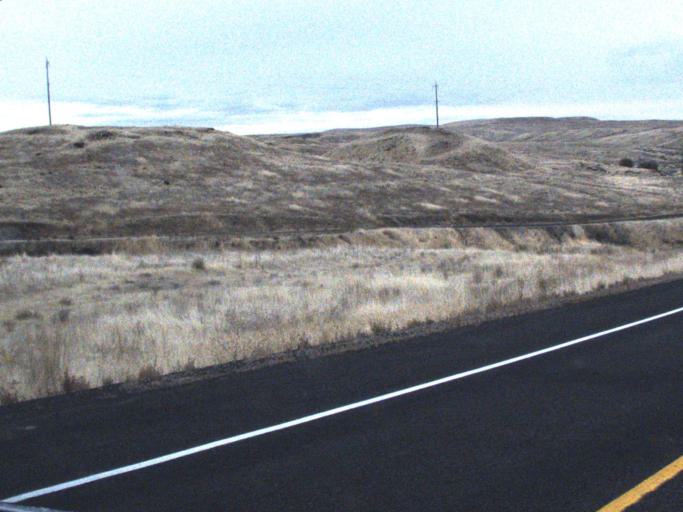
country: US
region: Washington
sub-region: Adams County
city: Ritzville
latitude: 46.7591
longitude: -118.3225
